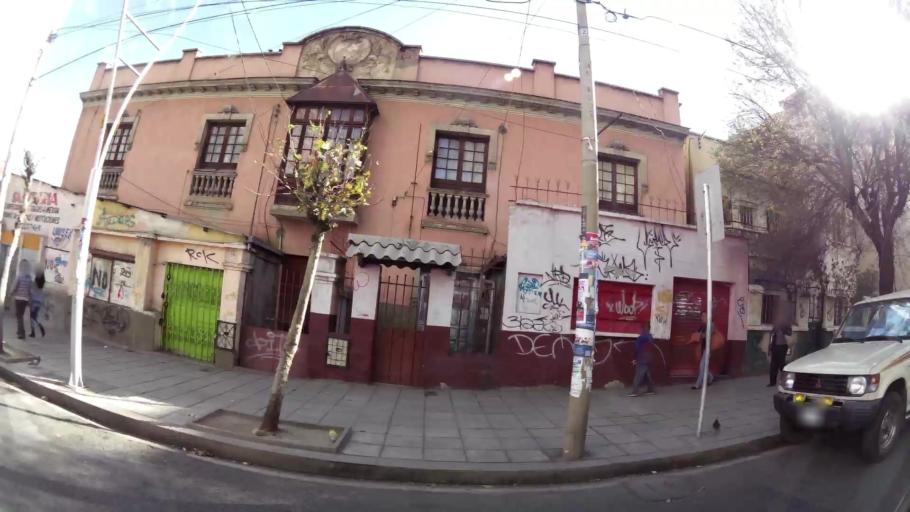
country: BO
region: La Paz
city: La Paz
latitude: -16.5032
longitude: -68.1219
